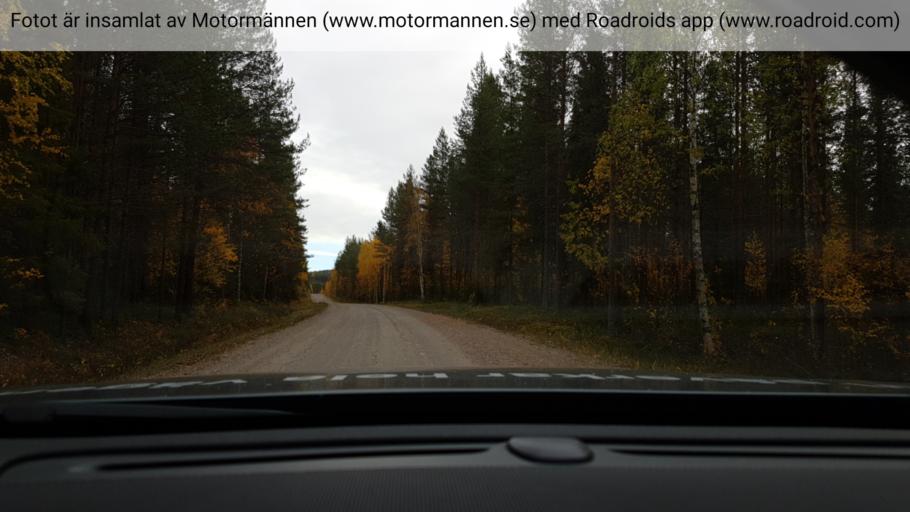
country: SE
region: Norrbotten
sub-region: Overkalix Kommun
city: OEverkalix
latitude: 66.2918
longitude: 22.9549
